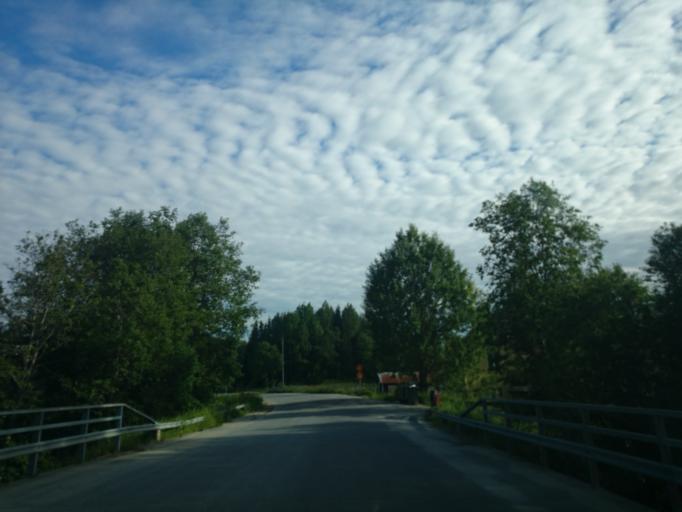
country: SE
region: Vaesternorrland
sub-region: Haernoesands Kommun
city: Haernoesand
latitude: 62.6370
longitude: 17.8467
